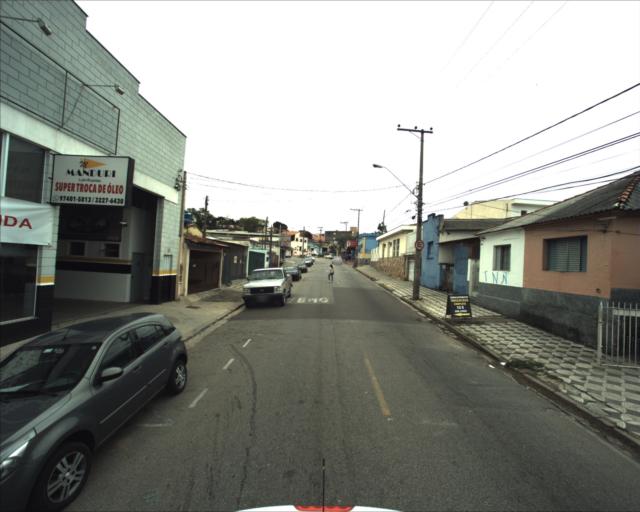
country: BR
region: Sao Paulo
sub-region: Sorocaba
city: Sorocaba
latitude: -23.5126
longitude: -47.4404
